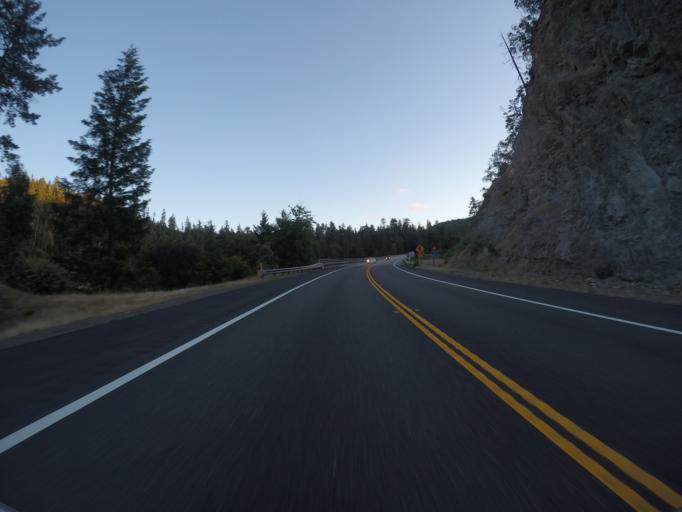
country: US
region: California
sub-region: Humboldt County
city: Redway
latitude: 39.9233
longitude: -123.7614
